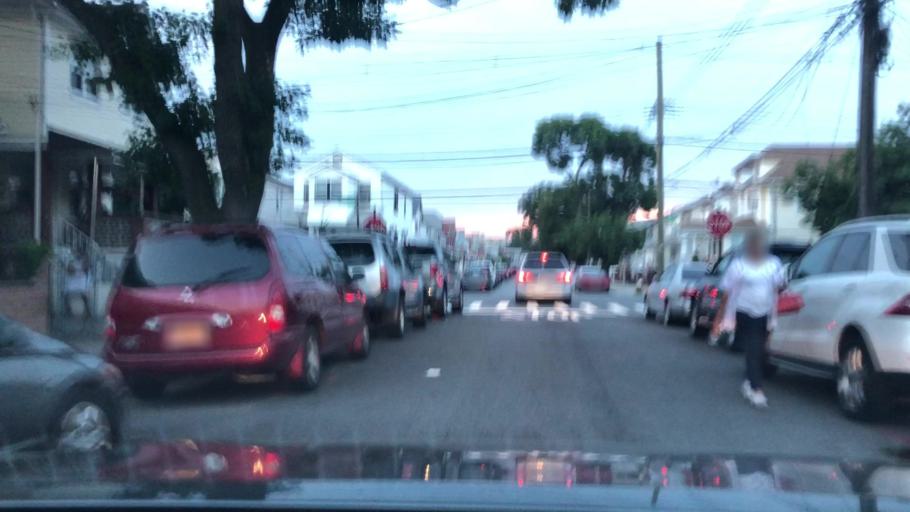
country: US
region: New York
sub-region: Queens County
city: Jamaica
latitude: 40.6849
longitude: -73.8205
